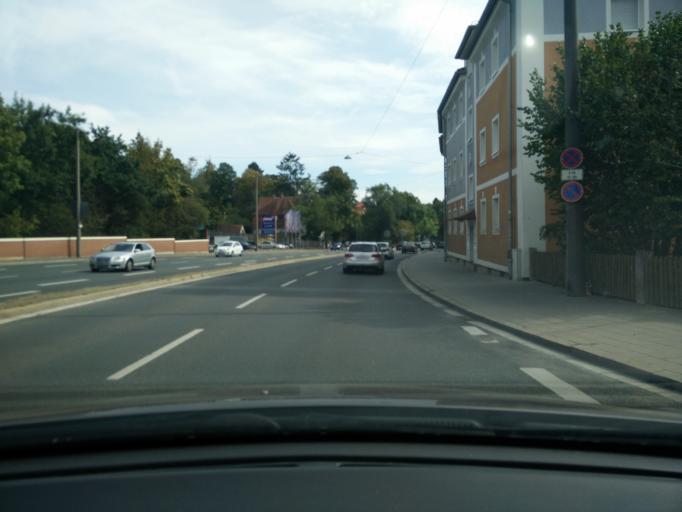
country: DE
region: Bavaria
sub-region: Regierungsbezirk Mittelfranken
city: Furth
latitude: 49.4817
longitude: 10.9700
